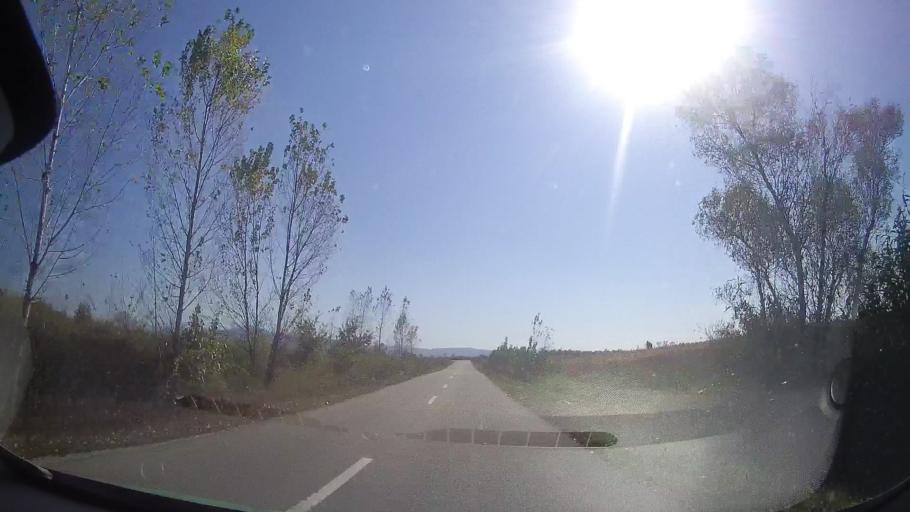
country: RO
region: Timis
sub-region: Comuna Traian Vuia
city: Traian Vuia
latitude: 45.7807
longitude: 22.0504
